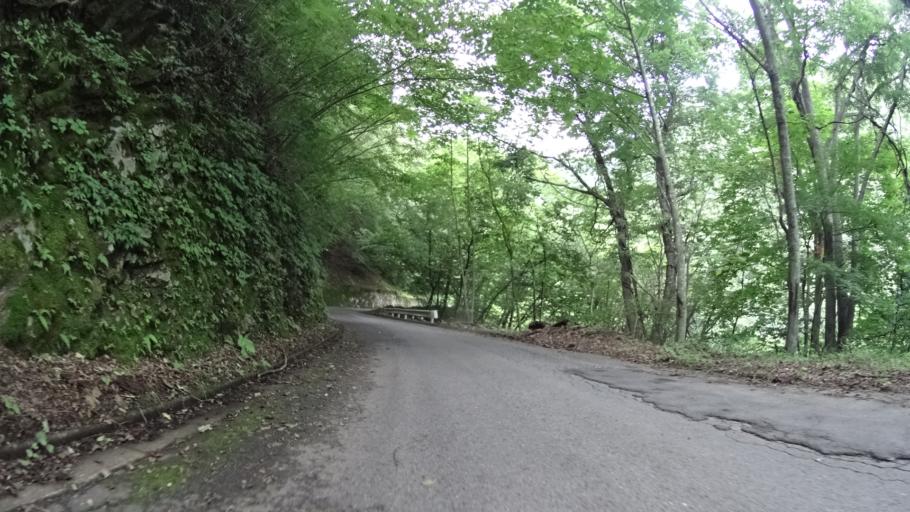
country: JP
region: Nagano
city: Saku
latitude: 36.0906
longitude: 138.6880
